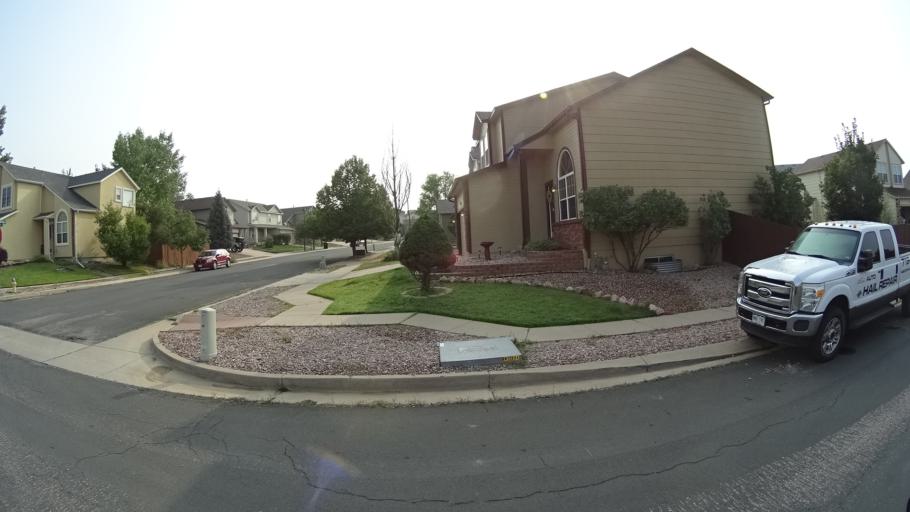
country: US
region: Colorado
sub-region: El Paso County
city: Black Forest
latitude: 38.9362
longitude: -104.7266
